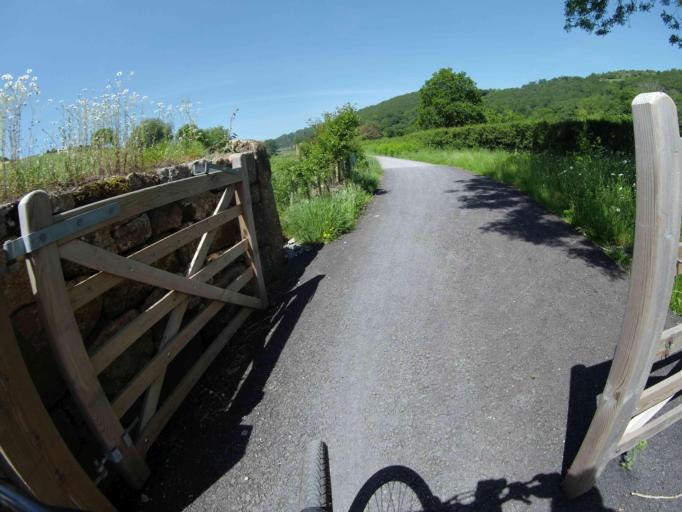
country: GB
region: England
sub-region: Devon
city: Bovey Tracey
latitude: 50.6446
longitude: -3.7397
